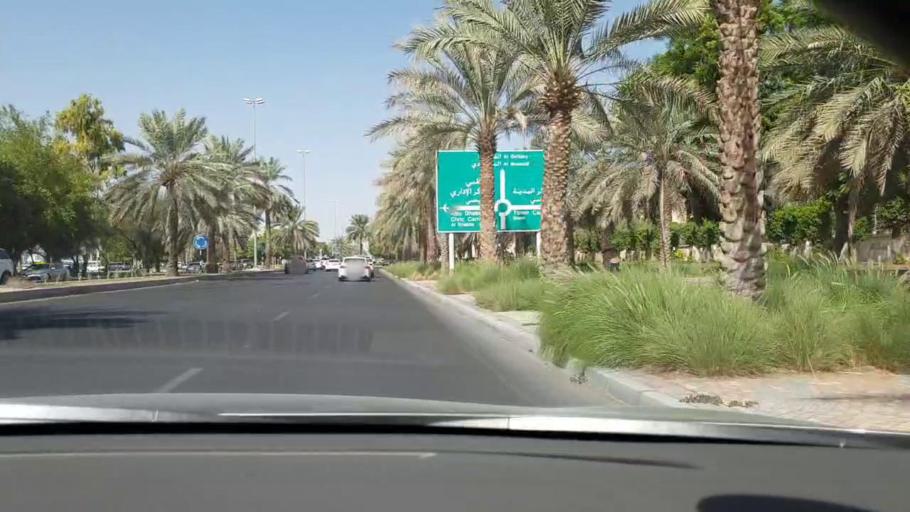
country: AE
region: Abu Dhabi
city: Al Ain
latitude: 24.2397
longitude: 55.7390
